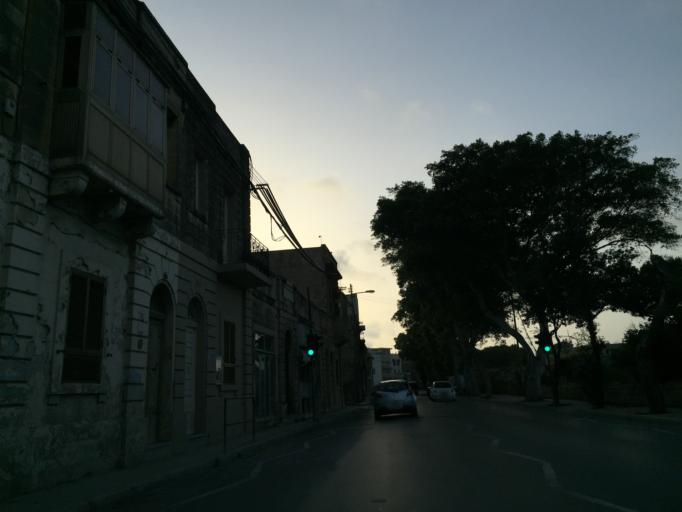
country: MT
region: Saint Paul's Bay
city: San Pawl il-Bahar
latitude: 35.9364
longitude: 14.4133
